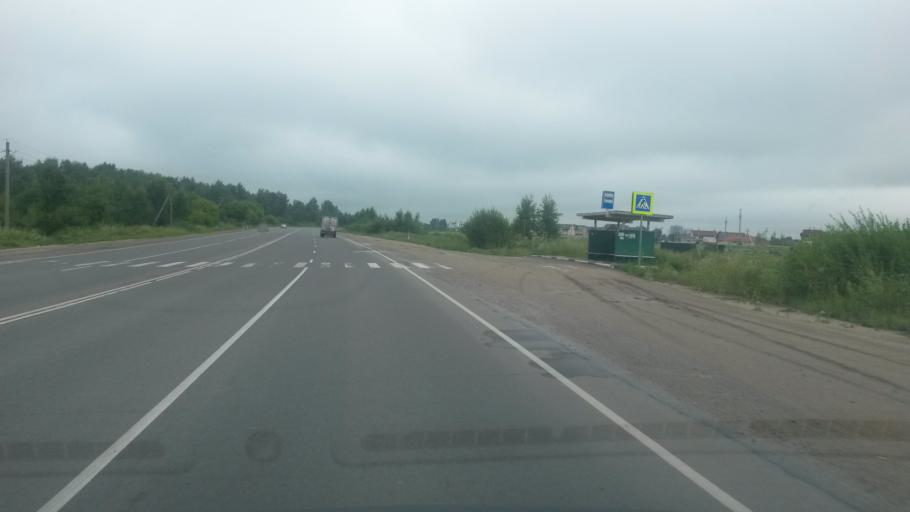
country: RU
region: Ivanovo
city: Novo-Talitsy
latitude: 57.0162
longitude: 40.8868
